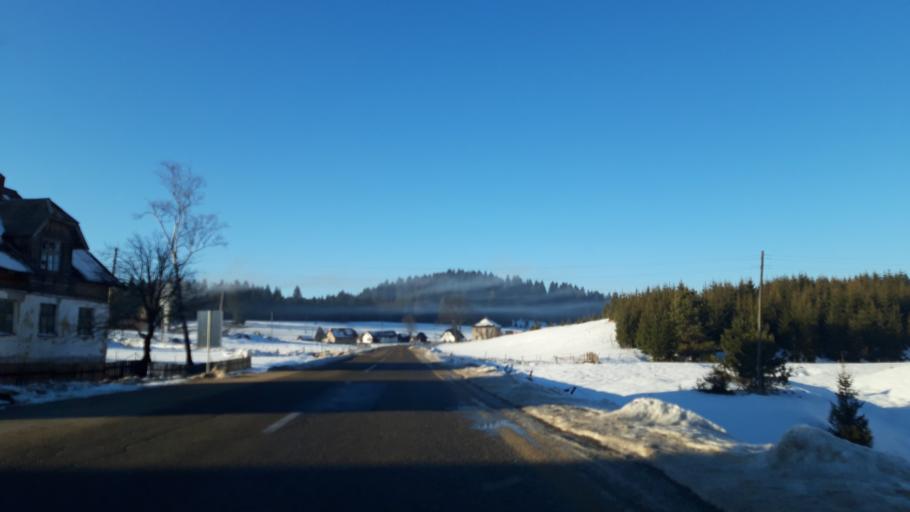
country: BA
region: Republika Srpska
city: Han Pijesak
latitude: 44.1079
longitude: 18.9702
